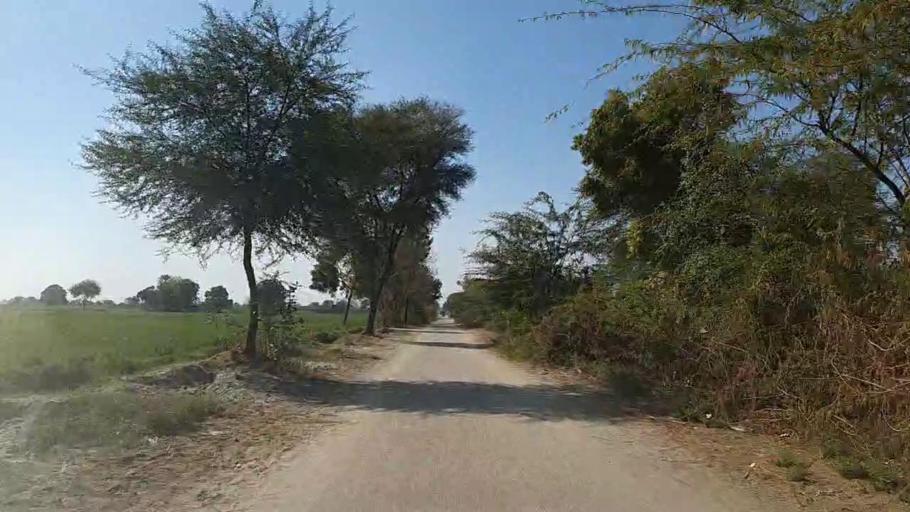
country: PK
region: Sindh
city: Nawabshah
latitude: 26.2448
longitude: 68.4392
